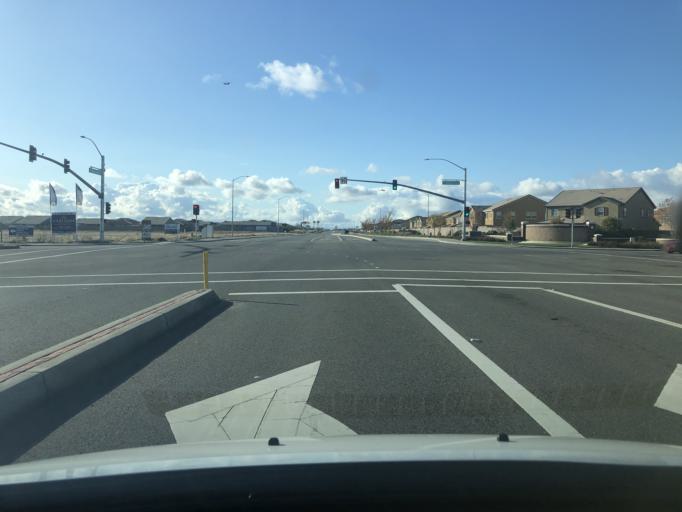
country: US
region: California
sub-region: Sacramento County
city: Antelope
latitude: 38.7754
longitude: -121.3847
